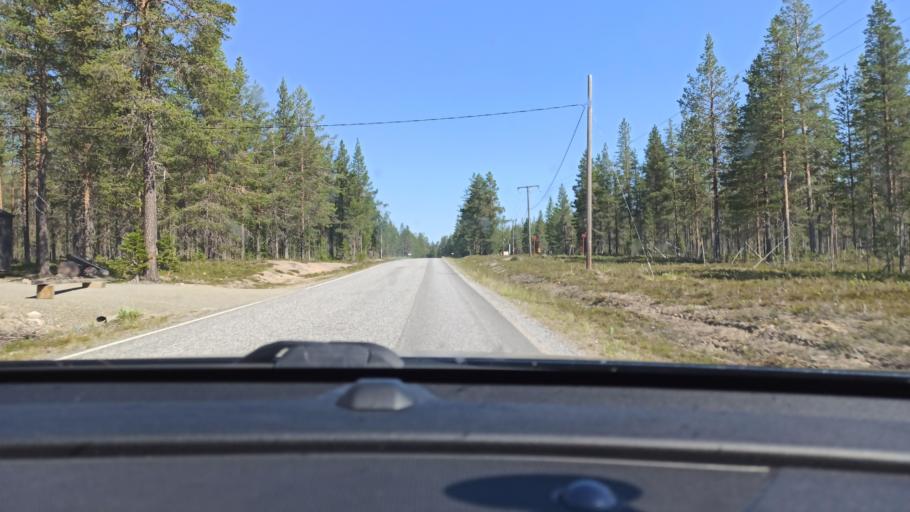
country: FI
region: Lapland
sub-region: Tunturi-Lappi
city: Kolari
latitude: 67.6541
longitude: 24.1635
